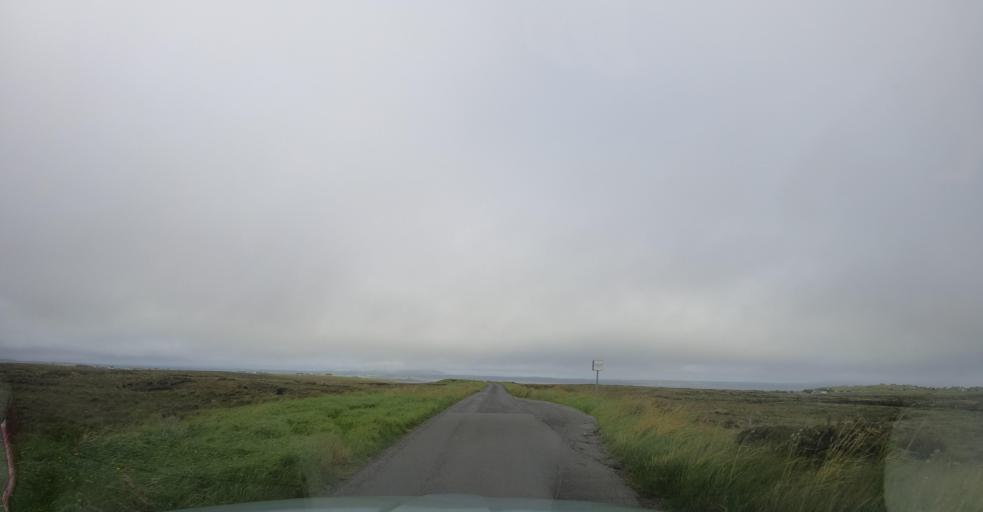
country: GB
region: Scotland
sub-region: Eilean Siar
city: Stornoway
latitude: 58.2032
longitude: -6.2413
